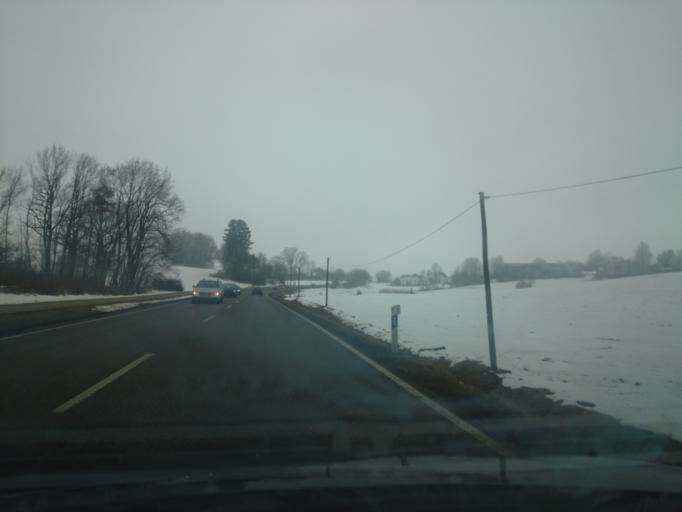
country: DE
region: Bavaria
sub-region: Swabia
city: Dasing
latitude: 48.3778
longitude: 11.0131
